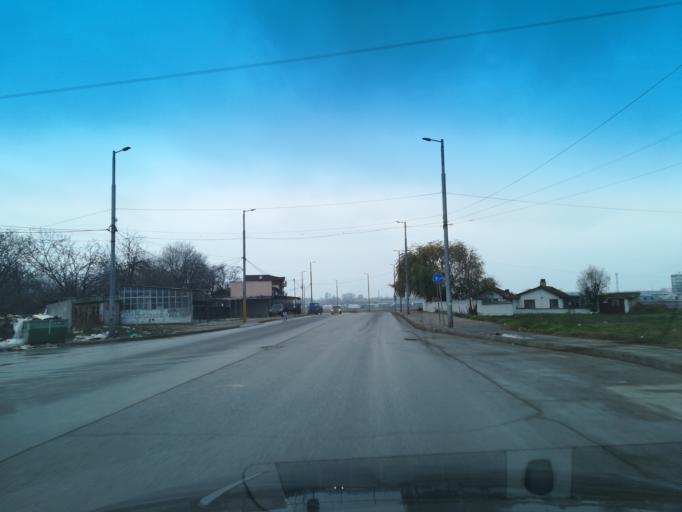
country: BG
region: Plovdiv
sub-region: Obshtina Plovdiv
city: Plovdiv
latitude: 42.1598
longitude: 24.7813
